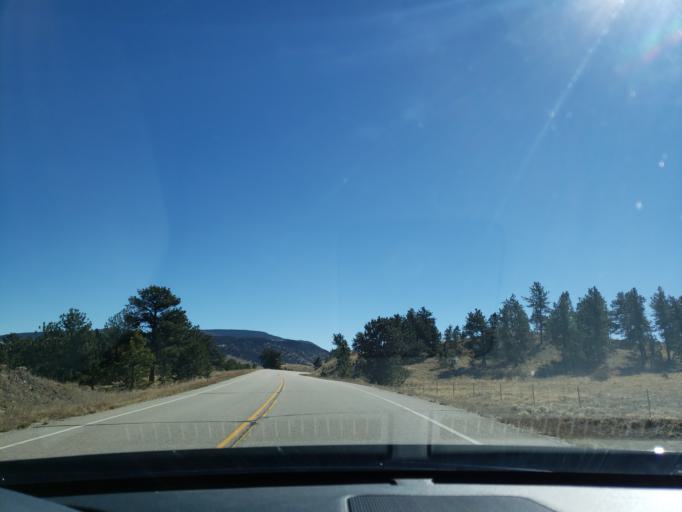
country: US
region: Colorado
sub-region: Chaffee County
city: Buena Vista
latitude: 38.8780
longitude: -105.6756
